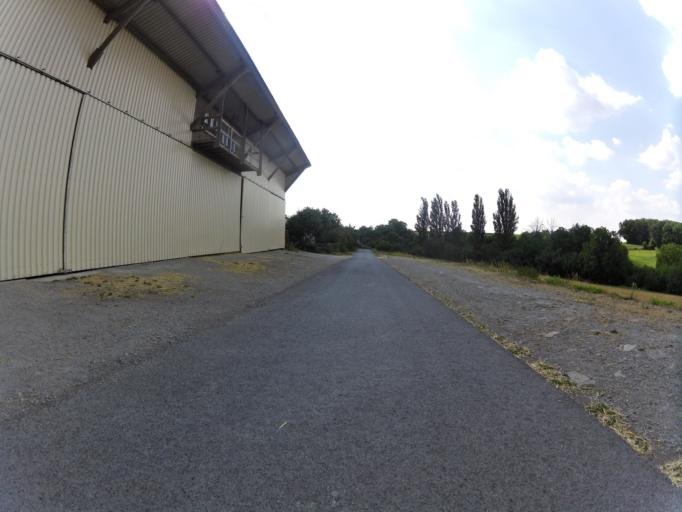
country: DE
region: Bavaria
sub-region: Regierungsbezirk Unterfranken
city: Ochsenfurt
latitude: 49.6521
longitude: 10.0739
